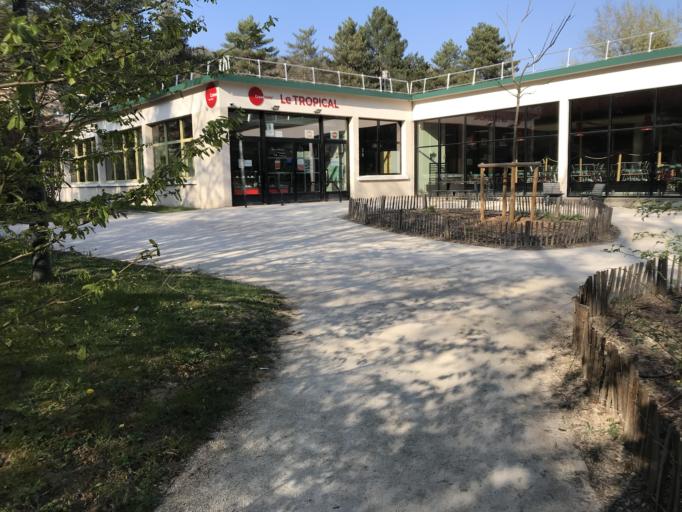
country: FR
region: Ile-de-France
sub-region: Departement de l'Essonne
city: Bures-sur-Yvette
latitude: 48.7024
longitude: 2.1789
